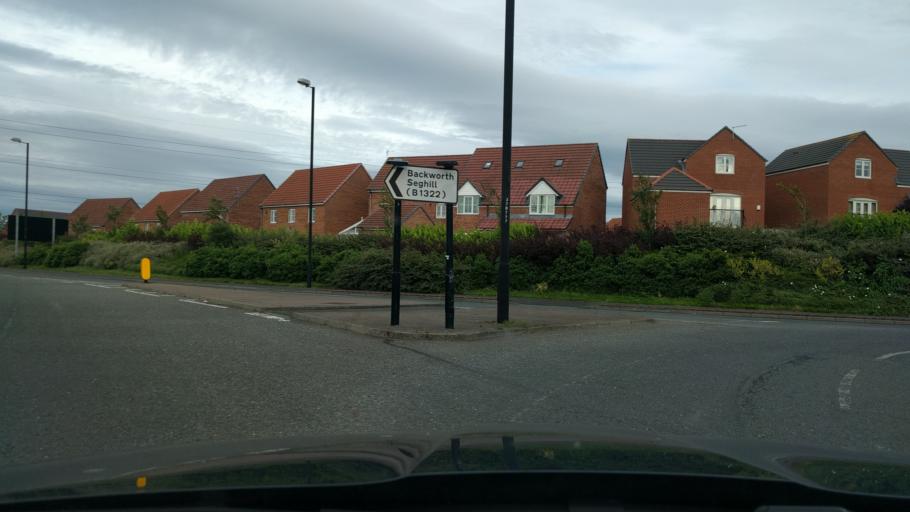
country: GB
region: England
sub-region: Borough of North Tyneside
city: Shiremoor
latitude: 55.0306
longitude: -1.5145
